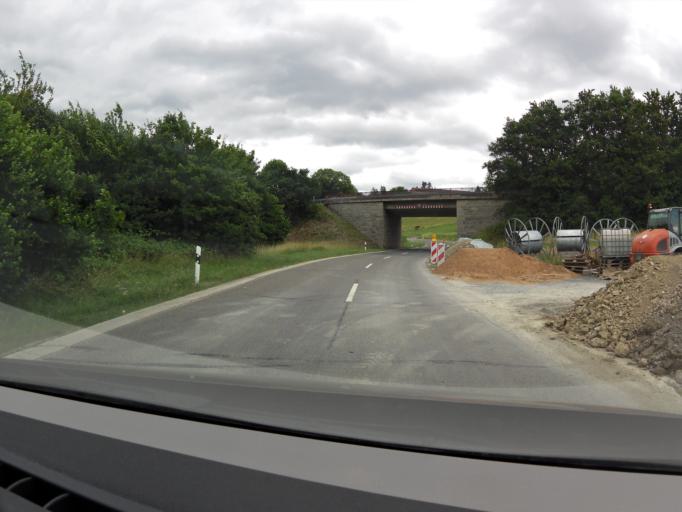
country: DE
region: Baden-Wuerttemberg
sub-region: Regierungsbezirk Stuttgart
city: Tauberbischofsheim
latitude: 49.6238
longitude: 9.6738
